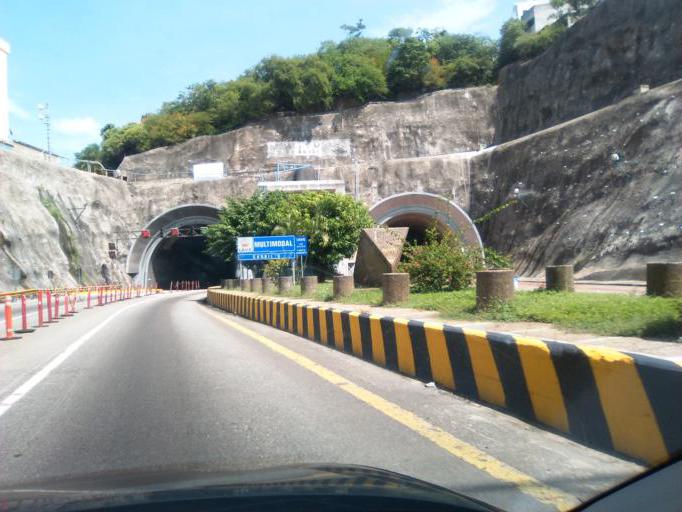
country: MX
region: Guerrero
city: Acapulco de Juarez
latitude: 16.8732
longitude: -99.8664
